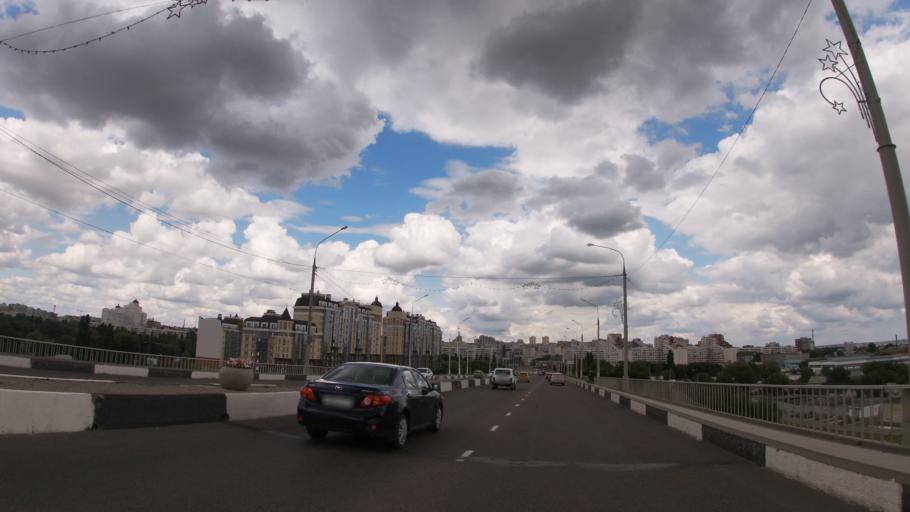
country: RU
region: Belgorod
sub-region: Belgorodskiy Rayon
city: Belgorod
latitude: 50.5865
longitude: 36.5875
